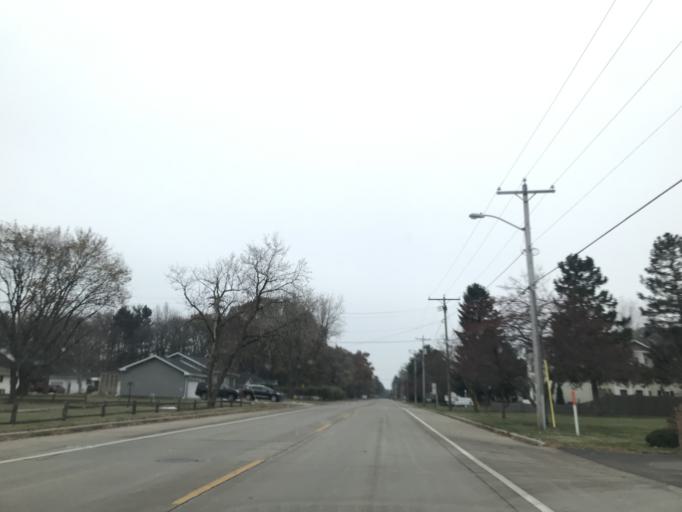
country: US
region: Wisconsin
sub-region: Marinette County
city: Marinette
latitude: 45.0750
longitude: -87.6194
